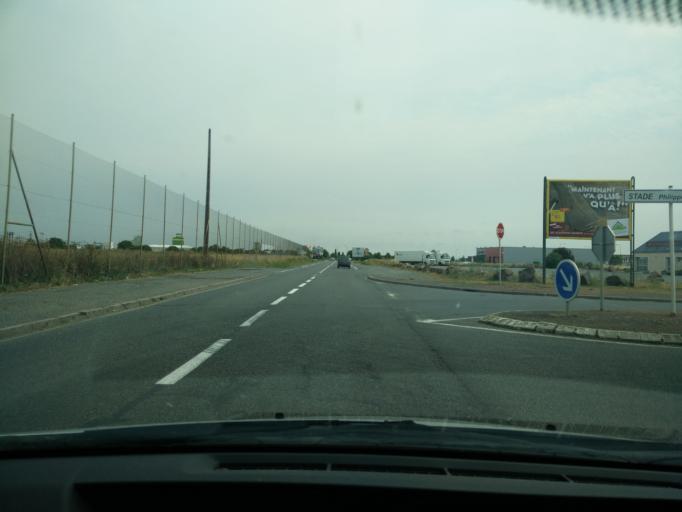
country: FR
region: Poitou-Charentes
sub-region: Departement des Deux-Sevres
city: Thouars
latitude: 46.9865
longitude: -0.1979
